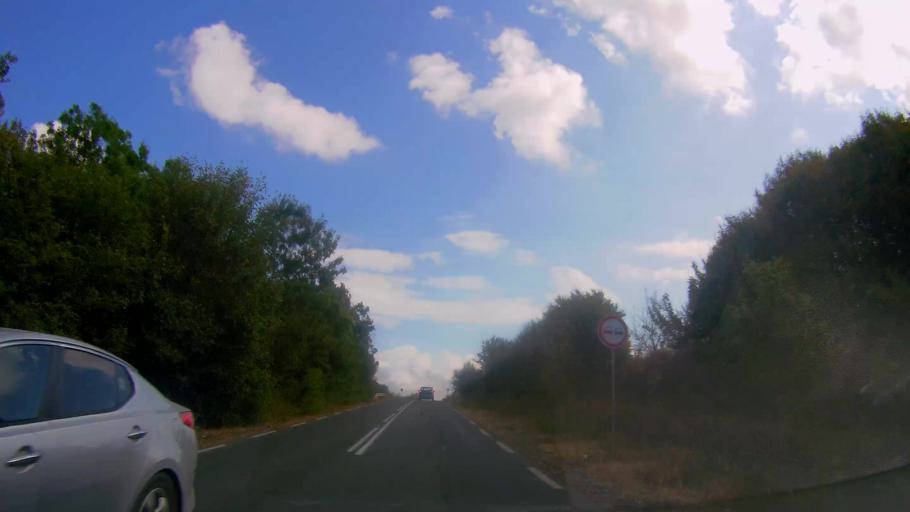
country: BG
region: Burgas
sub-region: Obshtina Kameno
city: Kameno
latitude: 42.4838
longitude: 27.3435
